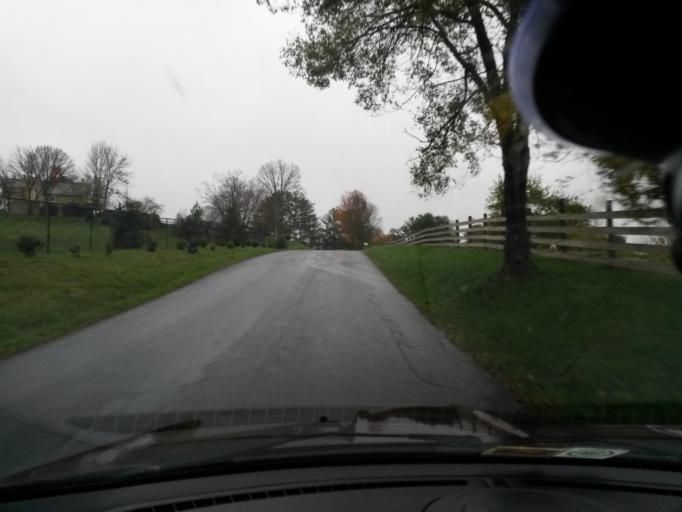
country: US
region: Virginia
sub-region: Botetourt County
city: Fincastle
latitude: 37.4936
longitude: -79.8764
